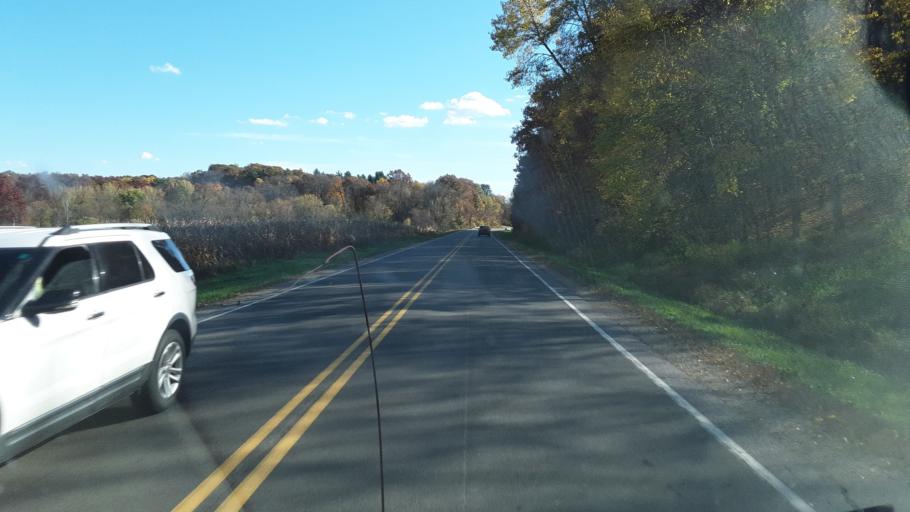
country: US
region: Wisconsin
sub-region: Sauk County
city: Reedsburg
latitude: 43.5750
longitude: -90.1337
